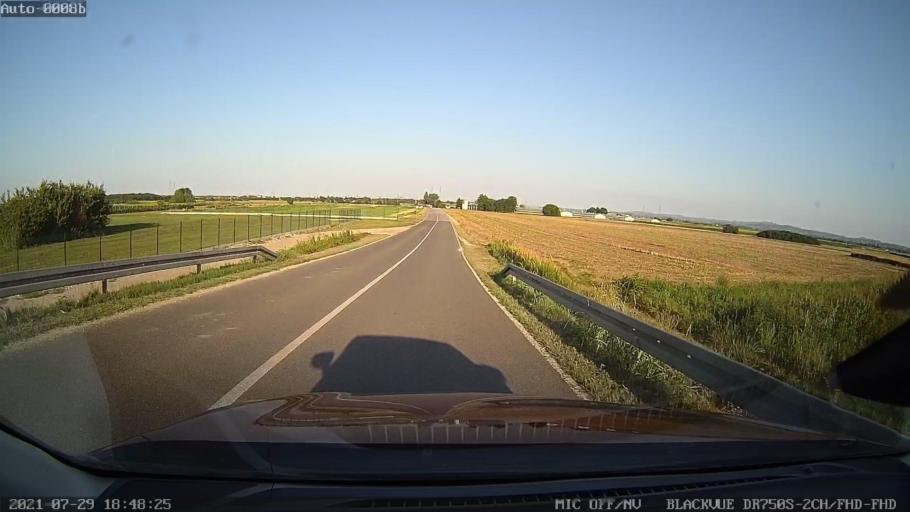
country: HR
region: Varazdinska
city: Sracinec
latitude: 46.3117
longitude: 16.2903
